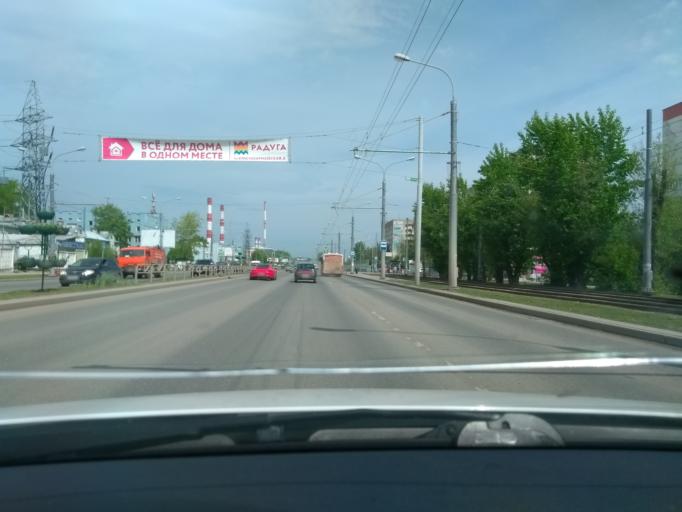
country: RU
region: Perm
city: Perm
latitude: 57.9690
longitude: 56.2618
